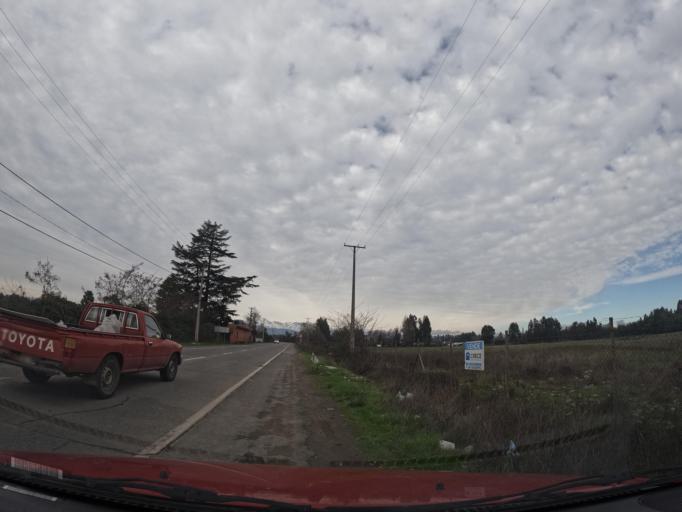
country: CL
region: Maule
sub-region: Provincia de Linares
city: Linares
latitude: -35.8632
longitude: -71.5625
